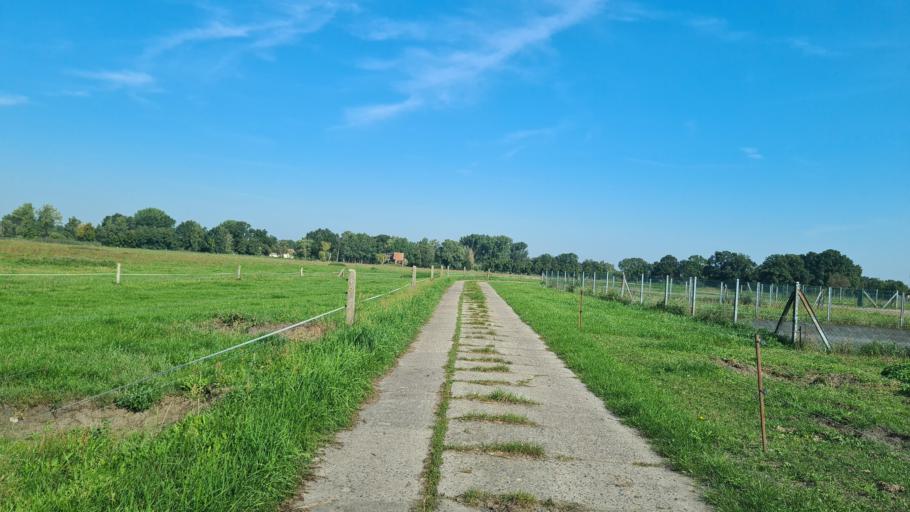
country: DE
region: Brandenburg
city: Friesack
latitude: 52.7765
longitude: 12.6066
